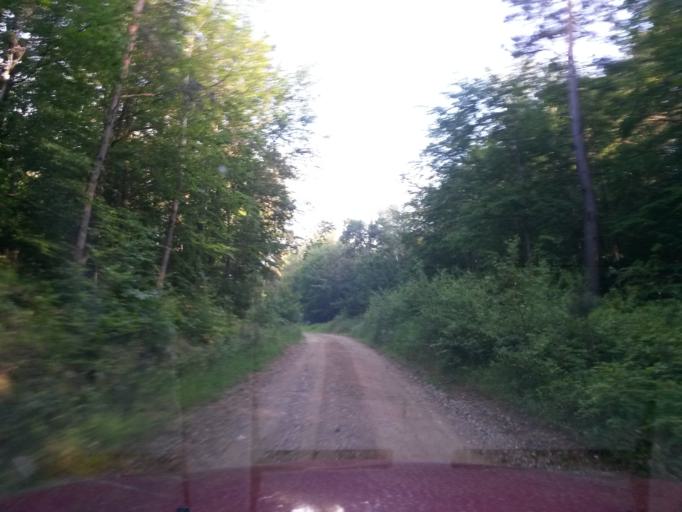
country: SK
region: Kosicky
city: Moldava nad Bodvou
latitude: 48.7441
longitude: 21.0272
